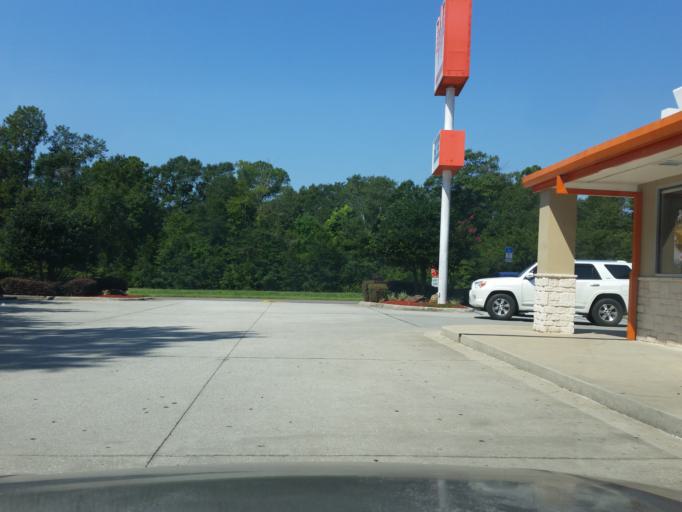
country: US
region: Florida
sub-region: Escambia County
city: Gonzalez
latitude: 30.5685
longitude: -87.2894
